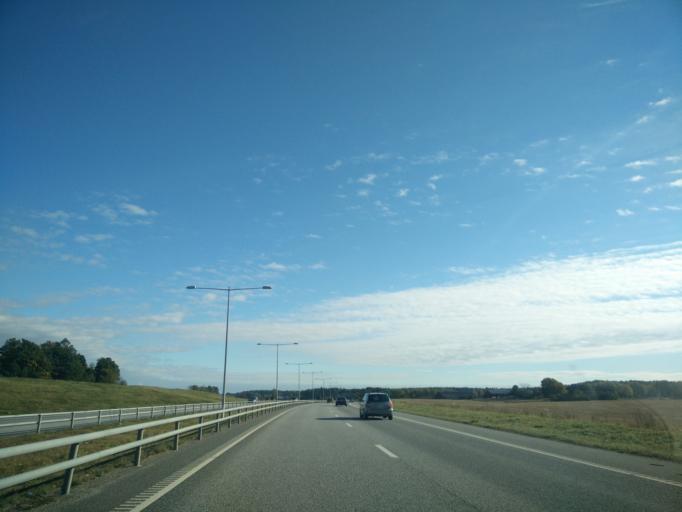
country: SE
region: Stockholm
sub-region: Taby Kommun
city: Taby
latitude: 59.4755
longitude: 18.0269
